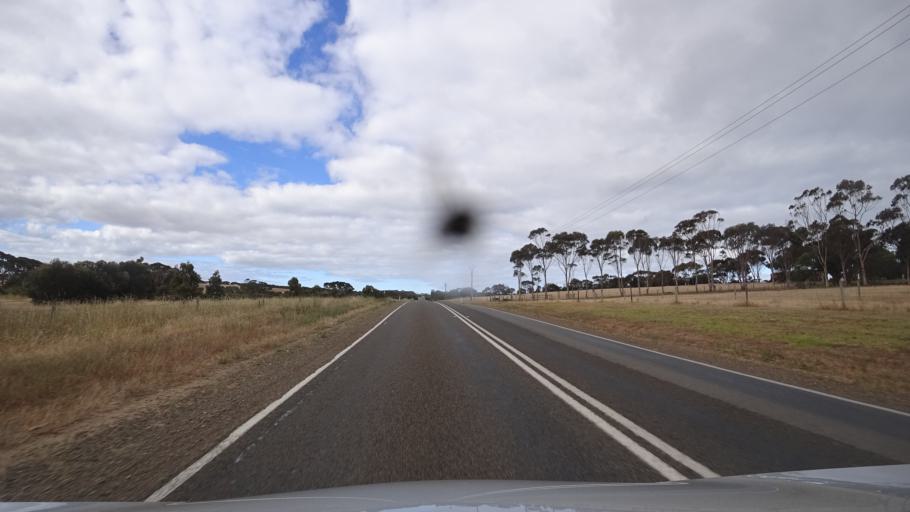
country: AU
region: South Australia
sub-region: Kangaroo Island
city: Kingscote
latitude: -35.6688
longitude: 137.5945
